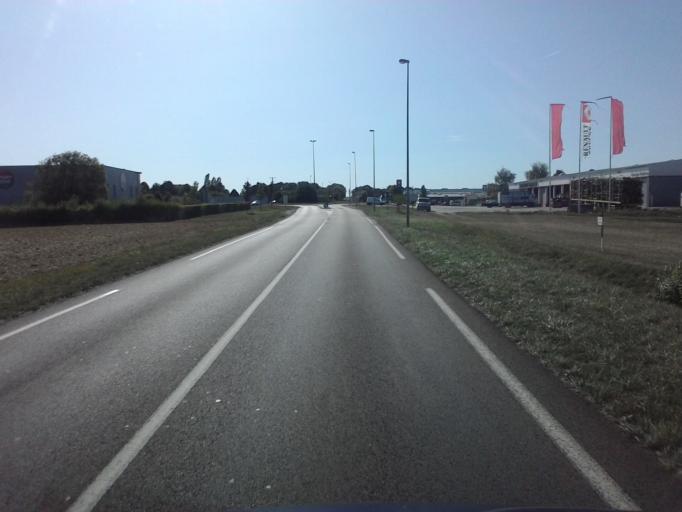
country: FR
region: Bourgogne
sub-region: Departement de la Cote-d'Or
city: Chatillon-sur-Seine
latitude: 47.8799
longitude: 4.5659
